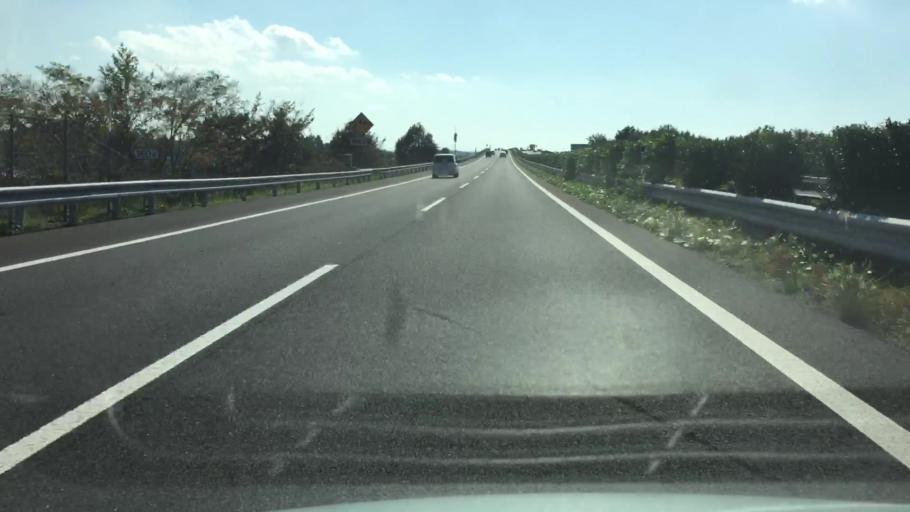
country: JP
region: Ibaraki
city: Tomobe
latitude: 36.3313
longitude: 140.2901
